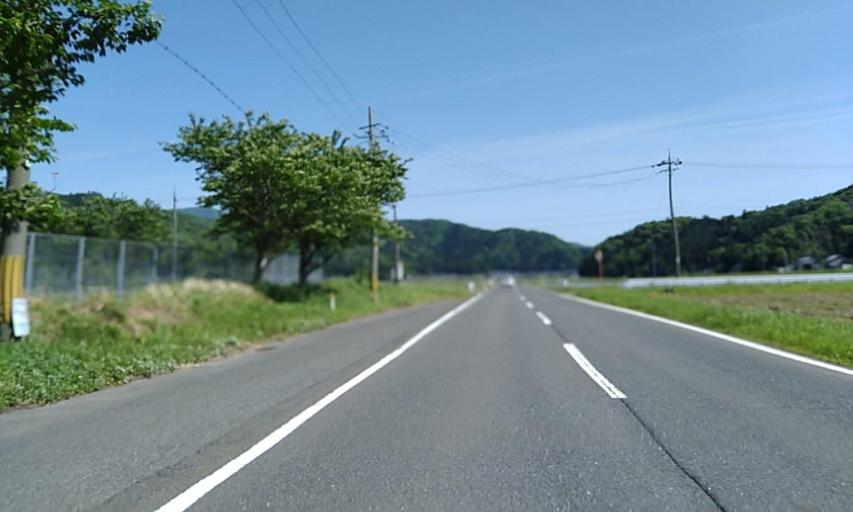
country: JP
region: Fukui
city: Obama
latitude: 35.5231
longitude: 135.8595
